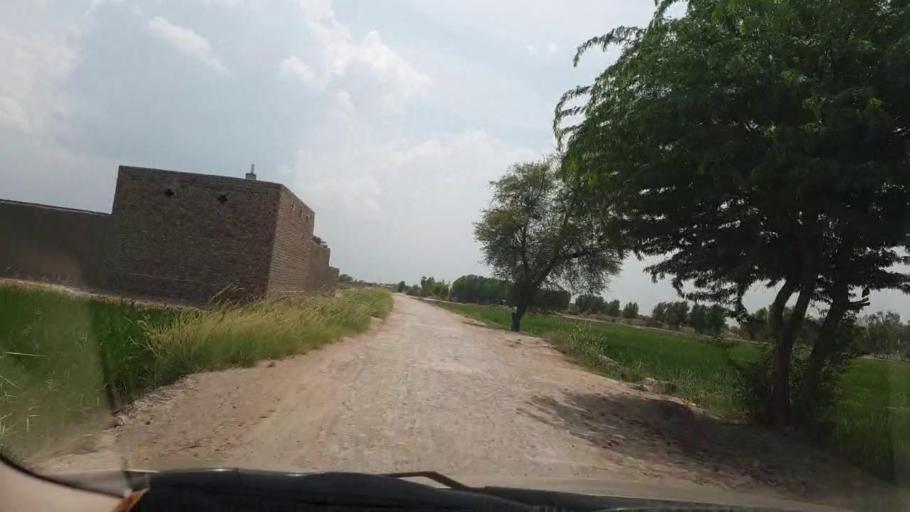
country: PK
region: Sindh
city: Larkana
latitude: 27.6181
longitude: 68.1549
